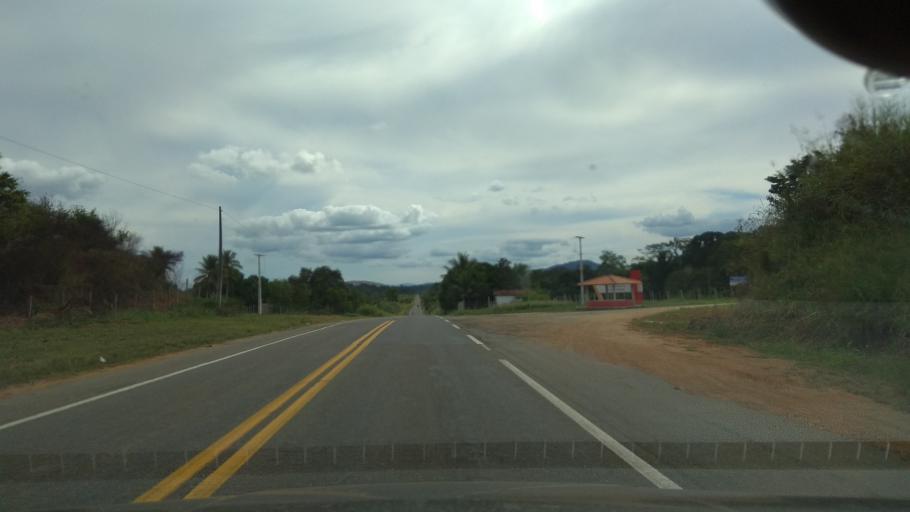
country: BR
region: Bahia
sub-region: Ubata
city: Ubata
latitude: -14.1964
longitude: -39.6254
